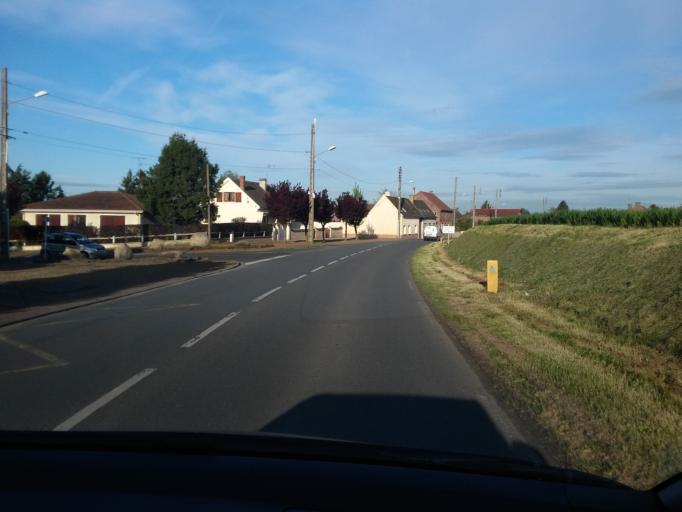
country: FR
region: Picardie
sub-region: Departement de l'Oise
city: Chevrieres
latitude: 49.3470
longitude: 2.6952
